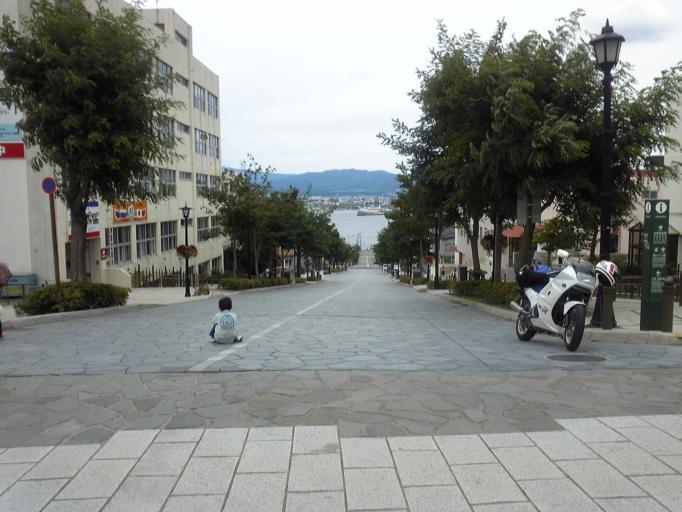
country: JP
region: Hokkaido
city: Hakodate
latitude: 41.7637
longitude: 140.7118
